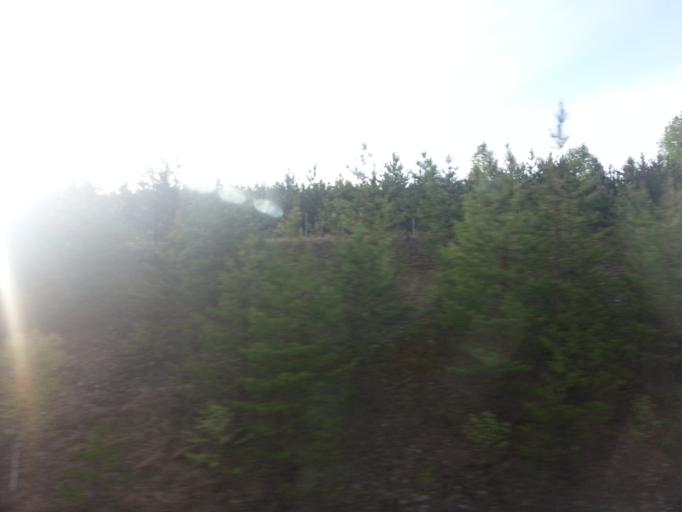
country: NO
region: Akershus
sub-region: Nannestad
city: Maura
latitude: 60.2152
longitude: 11.1092
